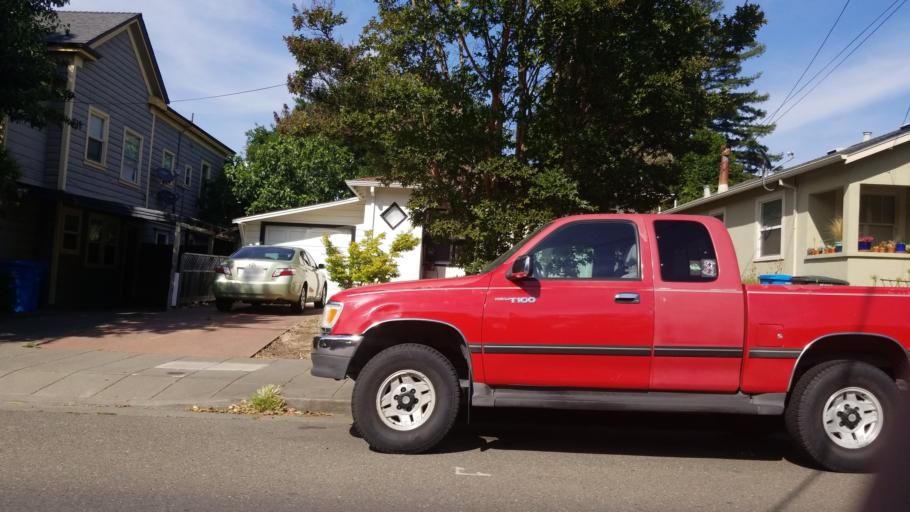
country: US
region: California
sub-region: Sonoma County
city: Santa Rosa
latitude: 38.4418
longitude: -122.7194
